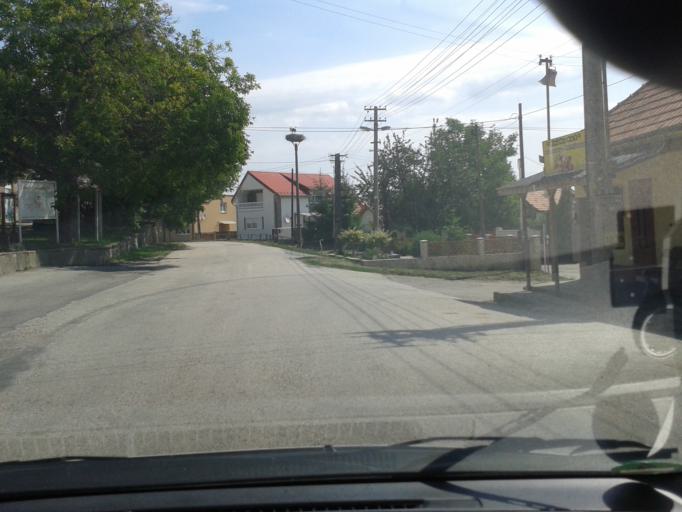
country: HU
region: Pest
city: Szob
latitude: 47.8297
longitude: 18.8277
